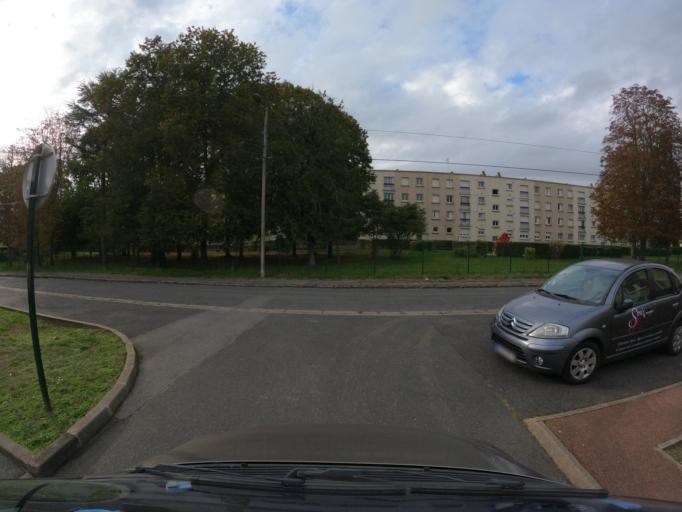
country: FR
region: Ile-de-France
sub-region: Departement de Seine-et-Marne
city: Chelles
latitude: 48.8795
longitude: 2.6014
